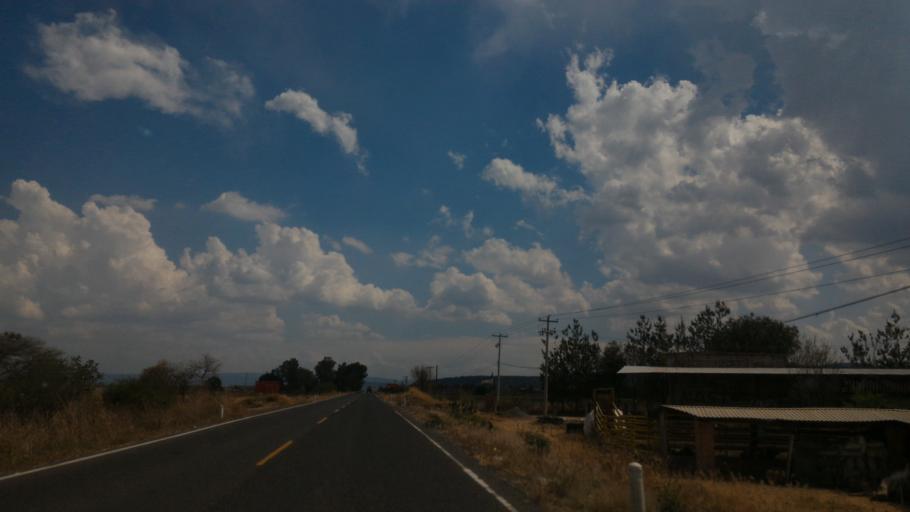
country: MX
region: Guanajuato
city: Ciudad Manuel Doblado
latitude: 20.7802
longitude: -101.9783
